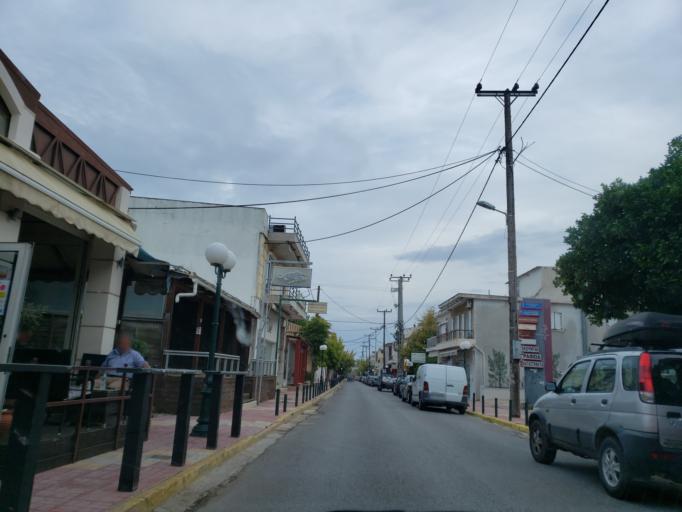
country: GR
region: Attica
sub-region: Nomarchia Anatolikis Attikis
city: Marathonas
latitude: 38.1563
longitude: 23.9600
